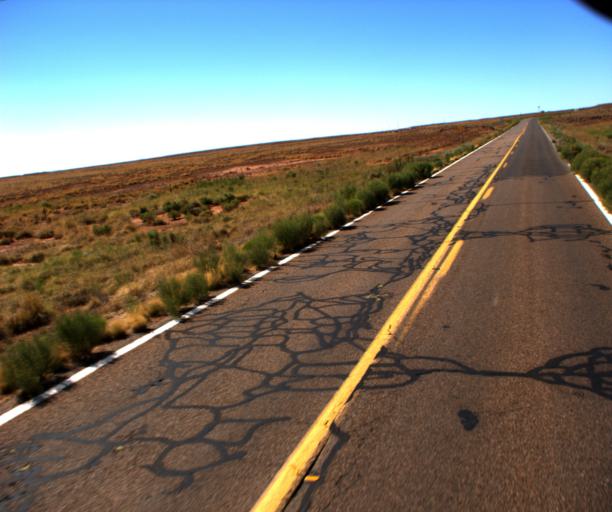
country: US
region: Arizona
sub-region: Coconino County
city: LeChee
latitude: 35.2544
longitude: -110.9620
